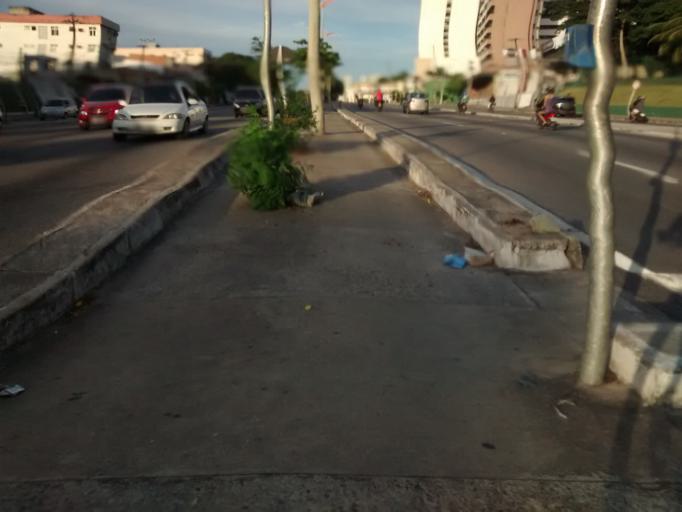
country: BR
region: Ceara
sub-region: Fortaleza
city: Fortaleza
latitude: -3.7370
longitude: -38.5719
